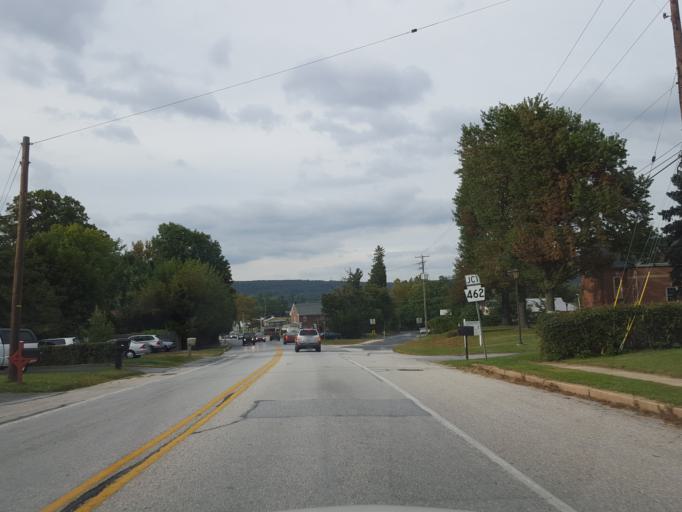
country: US
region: Pennsylvania
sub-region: York County
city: Stonybrook
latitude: 39.9751
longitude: -76.6601
